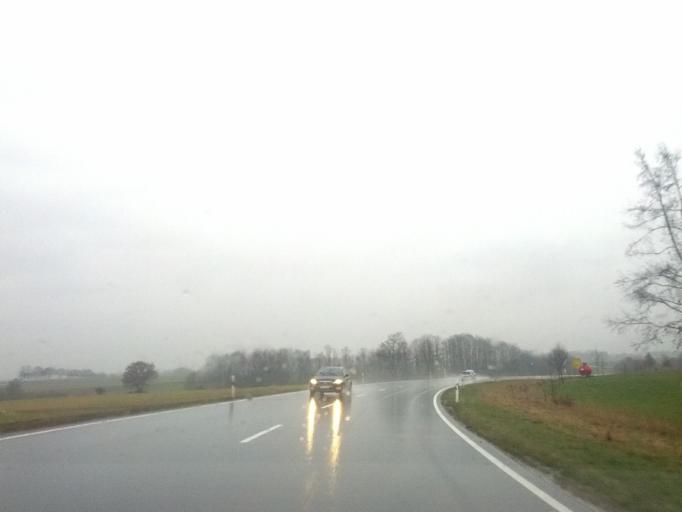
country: DE
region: Baden-Wuerttemberg
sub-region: Tuebingen Region
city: Ochsenhausen
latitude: 48.0748
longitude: 9.9144
